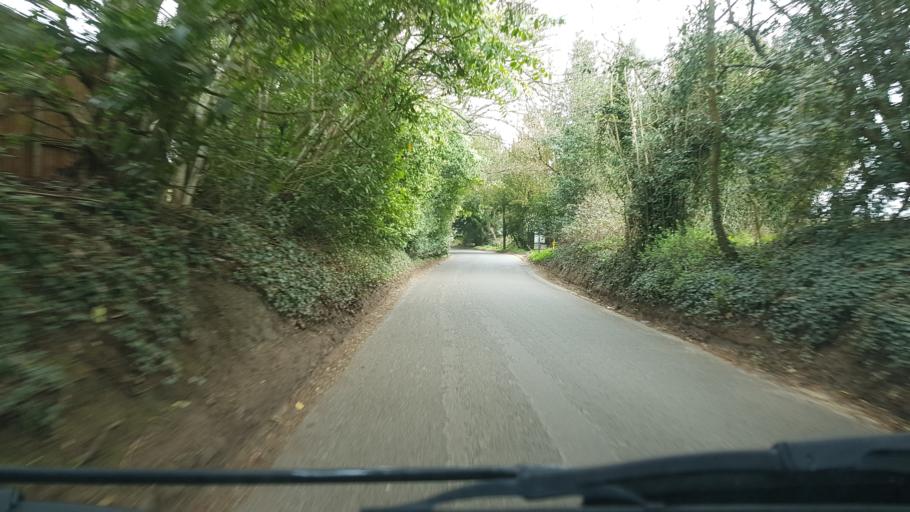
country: GB
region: England
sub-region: Surrey
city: Cranleigh
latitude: 51.1913
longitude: -0.4640
